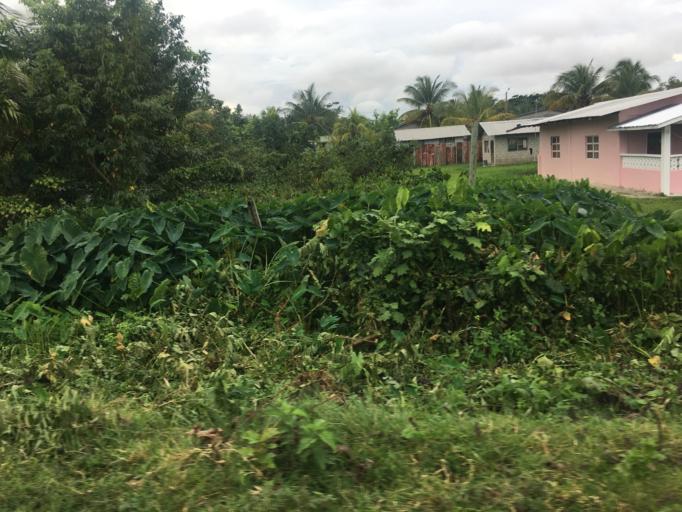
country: GY
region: Demerara-Mahaica
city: Georgetown
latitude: 6.7934
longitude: -58.1328
